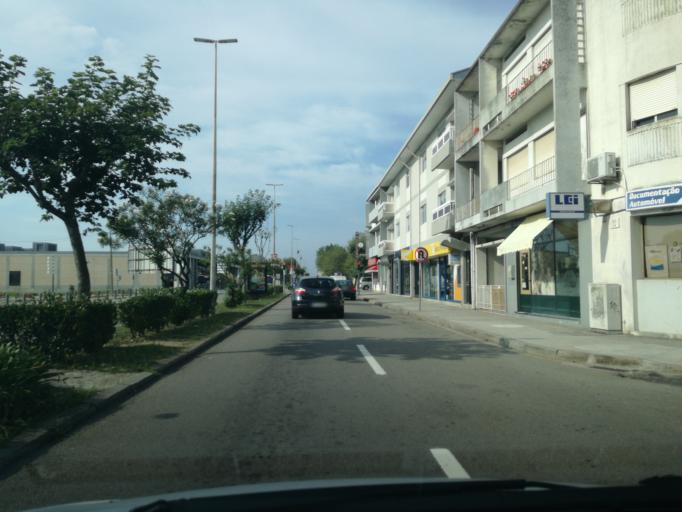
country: PT
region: Aveiro
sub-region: Espinho
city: Espinho
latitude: 41.0066
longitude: -8.6380
